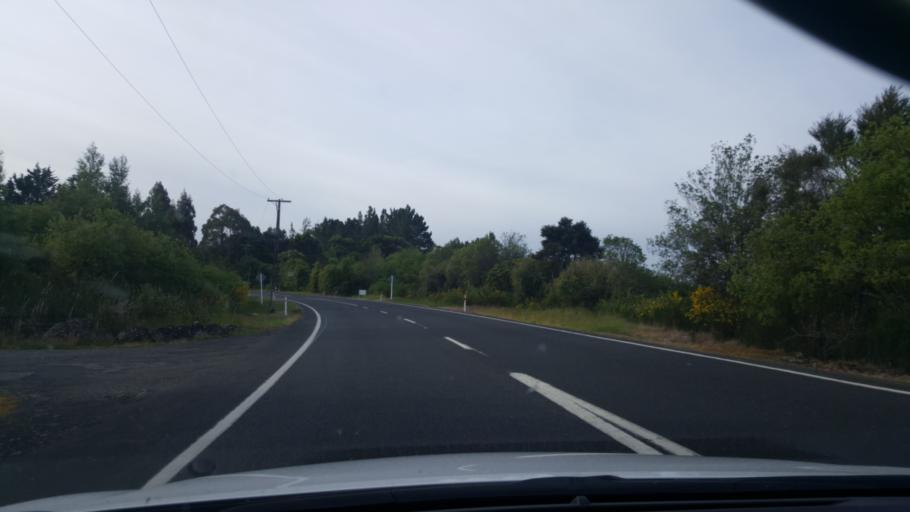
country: NZ
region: Waikato
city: Turangi
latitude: -38.9618
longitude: 175.7648
